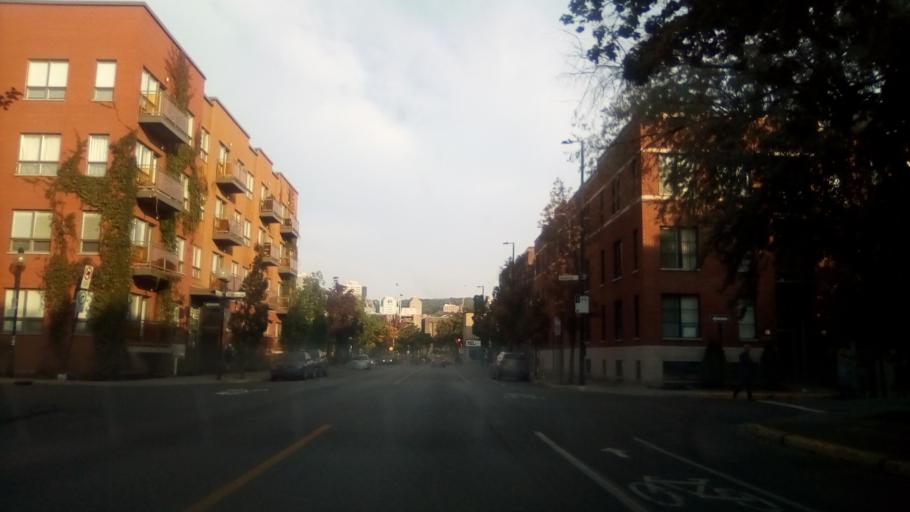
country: CA
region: Quebec
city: Westmount
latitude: 45.4819
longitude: -73.5748
